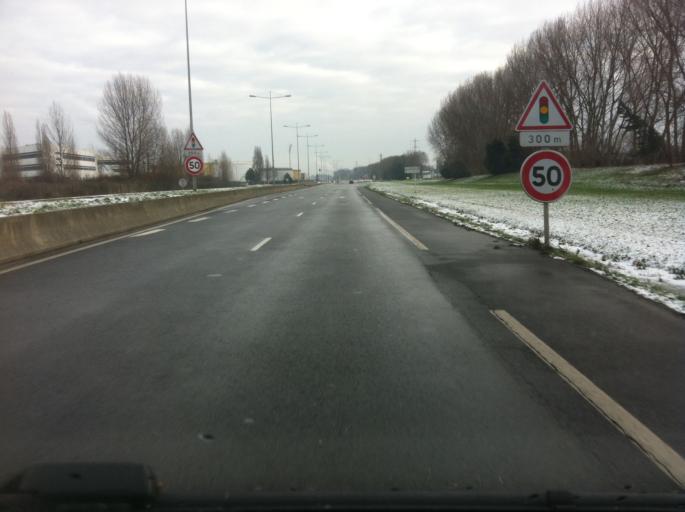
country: FR
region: Haute-Normandie
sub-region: Departement de la Seine-Maritime
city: Harfleur
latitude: 49.4862
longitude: 0.2200
